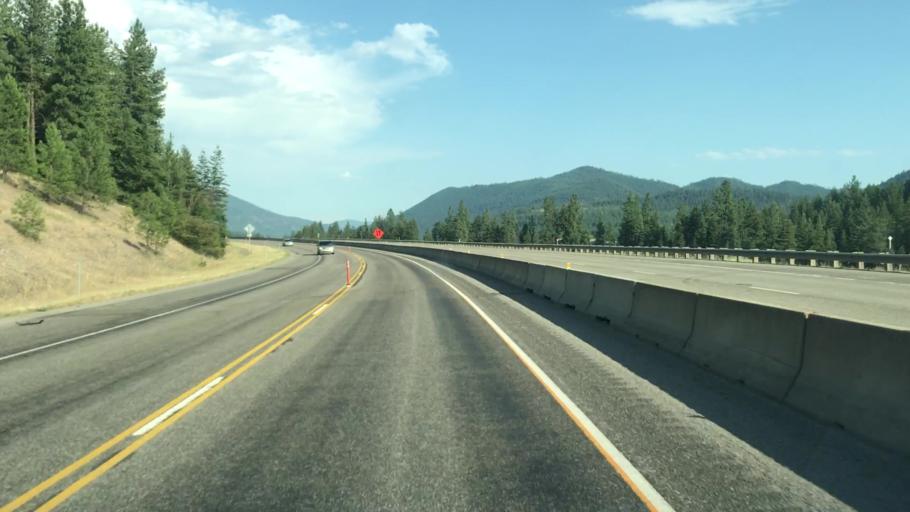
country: US
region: Montana
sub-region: Mineral County
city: Superior
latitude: 47.2185
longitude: -114.9572
